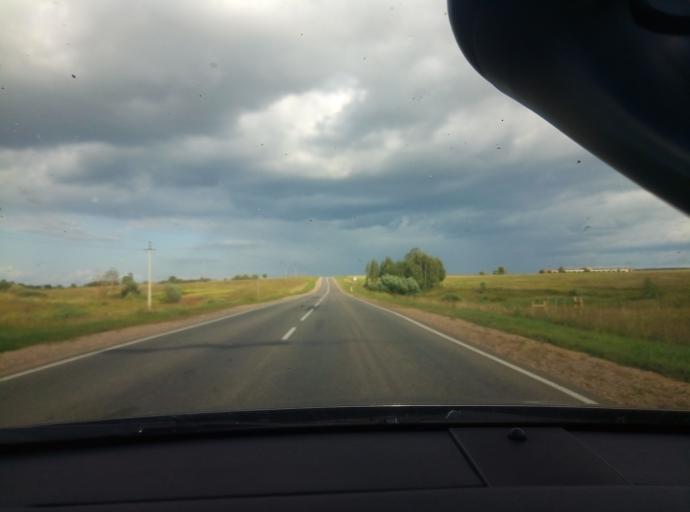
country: RU
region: Kaluga
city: Babynino
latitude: 54.5228
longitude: 35.6057
